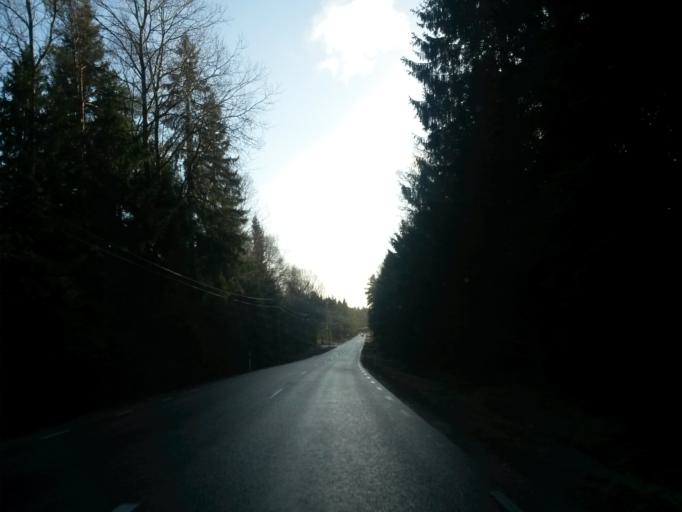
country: SE
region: Vaestra Goetaland
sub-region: Boras Kommun
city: Boras
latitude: 57.8921
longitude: 12.9258
